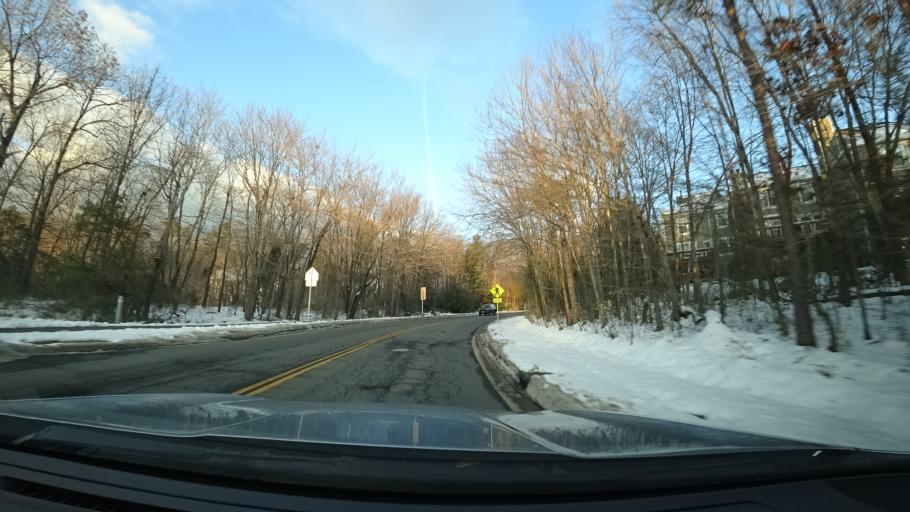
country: US
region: Virginia
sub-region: Fairfax County
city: Reston
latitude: 38.9798
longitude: -77.3570
